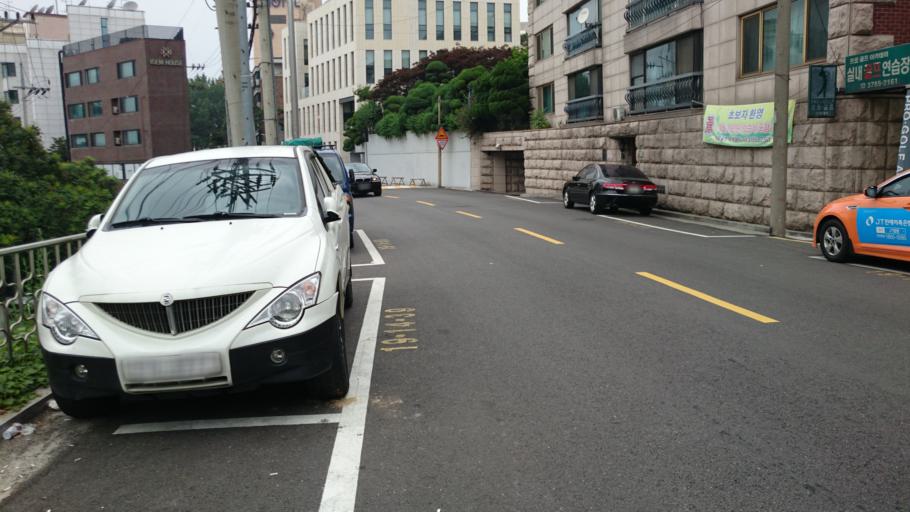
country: KR
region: Seoul
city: Seoul
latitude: 37.5275
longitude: 126.9951
